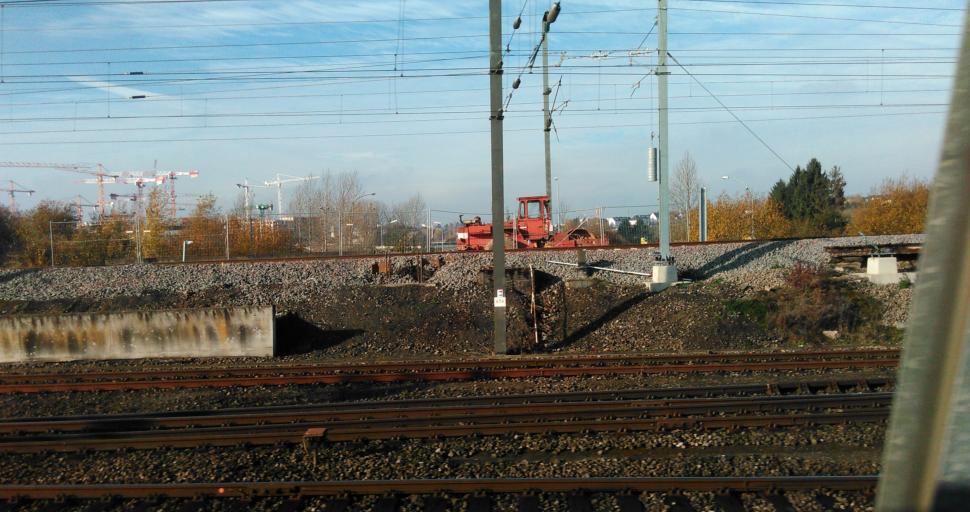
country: LU
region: Luxembourg
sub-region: Canton de Luxembourg
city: Hesperange
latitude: 49.5859
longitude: 6.1355
